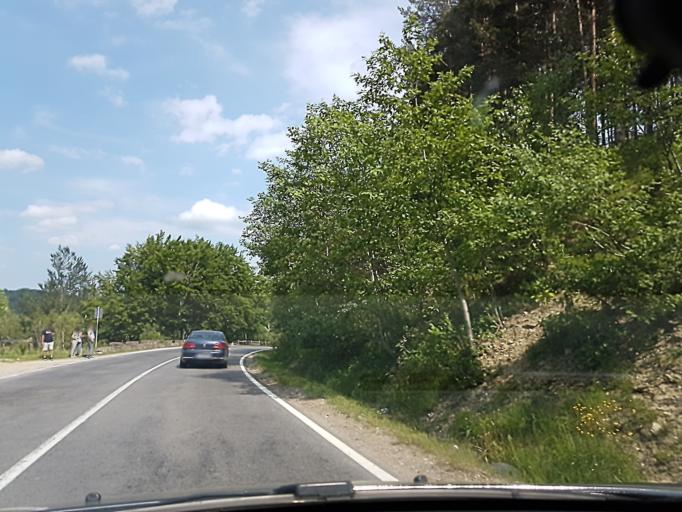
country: RO
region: Prahova
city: Maneciu
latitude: 45.3296
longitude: 25.9758
